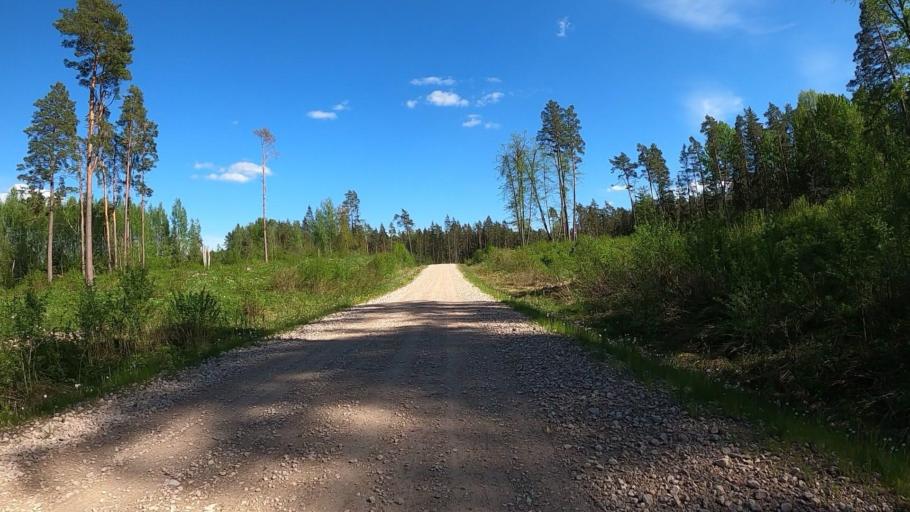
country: LV
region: Baldone
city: Baldone
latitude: 56.7898
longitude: 24.3374
